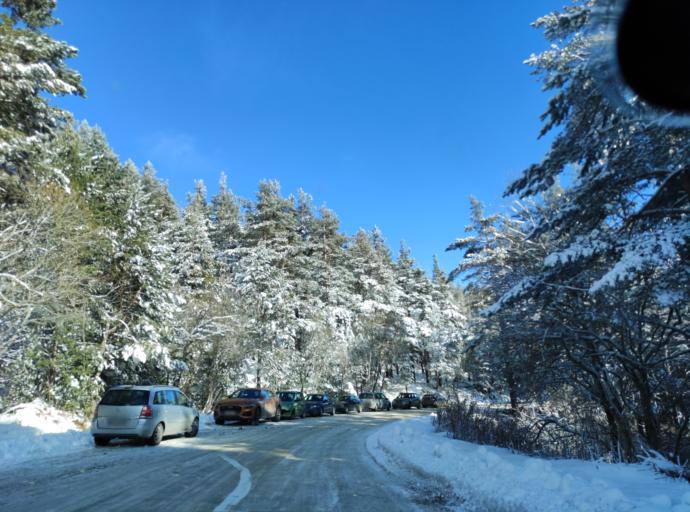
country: BG
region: Sofia-Capital
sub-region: Stolichna Obshtina
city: Sofia
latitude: 42.5901
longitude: 23.2936
